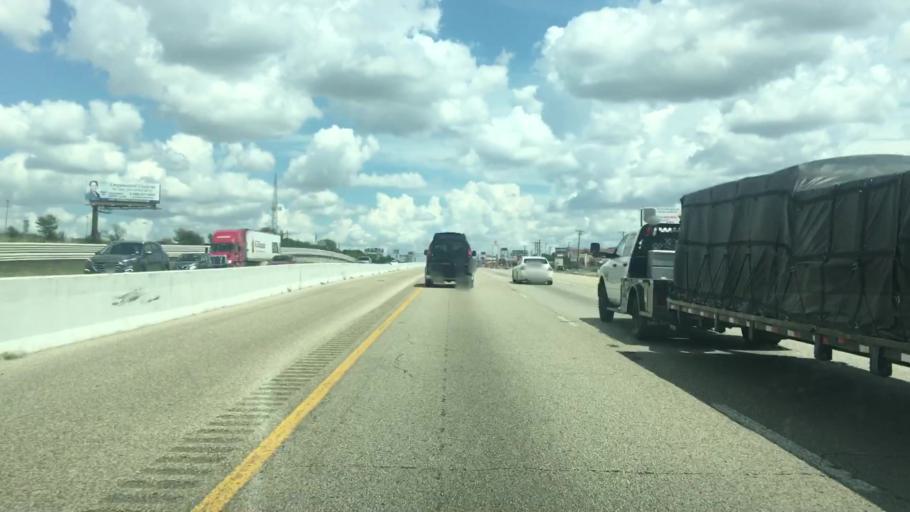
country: US
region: Texas
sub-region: Bell County
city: Temple
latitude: 31.0860
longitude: -97.4019
